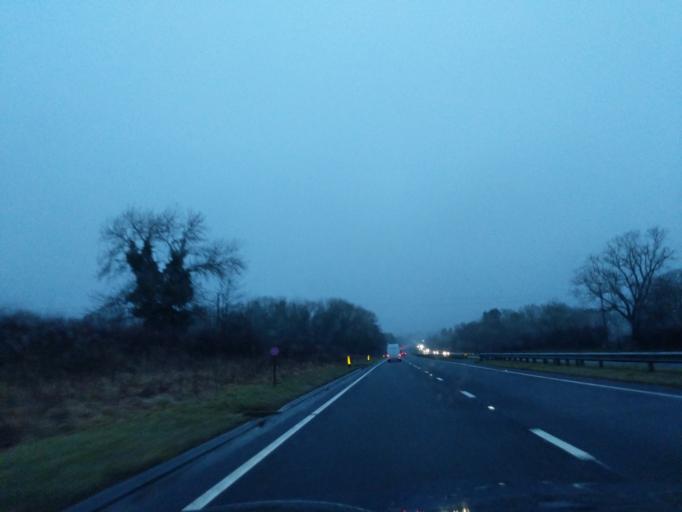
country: GB
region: England
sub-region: Northumberland
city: Felton
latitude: 55.3465
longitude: -1.7274
